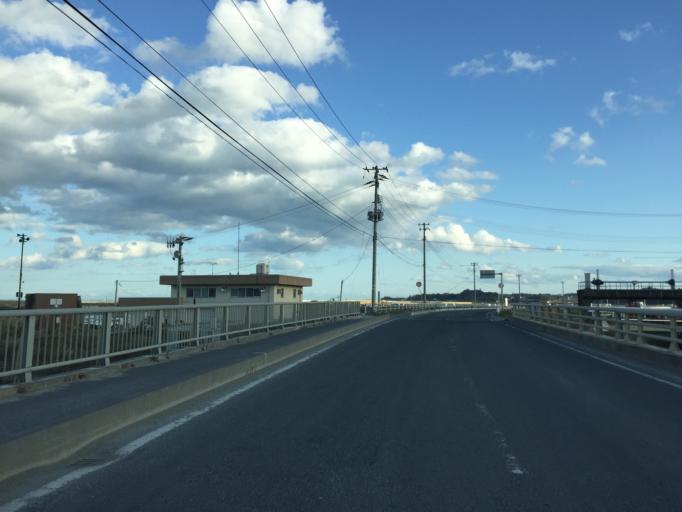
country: JP
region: Miyagi
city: Marumori
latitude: 37.7769
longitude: 140.9790
